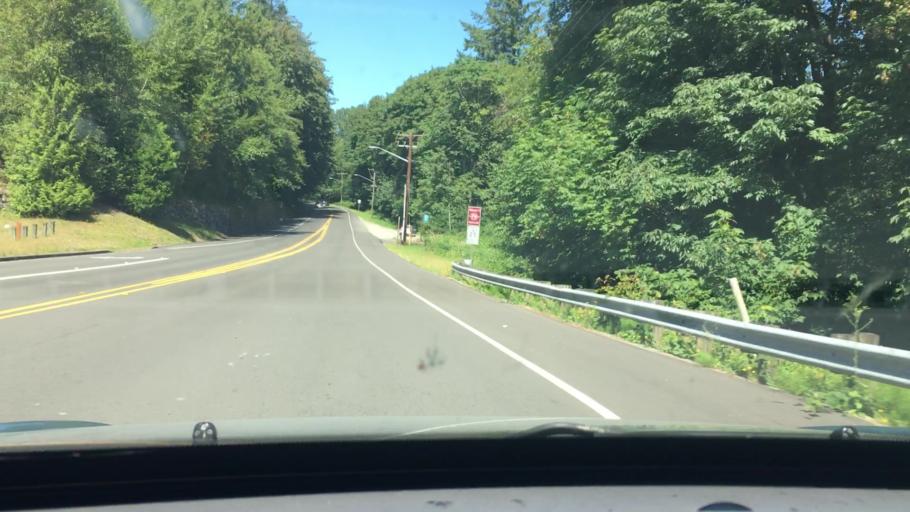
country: US
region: Washington
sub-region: King County
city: Newcastle
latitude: 47.5371
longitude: -122.1338
